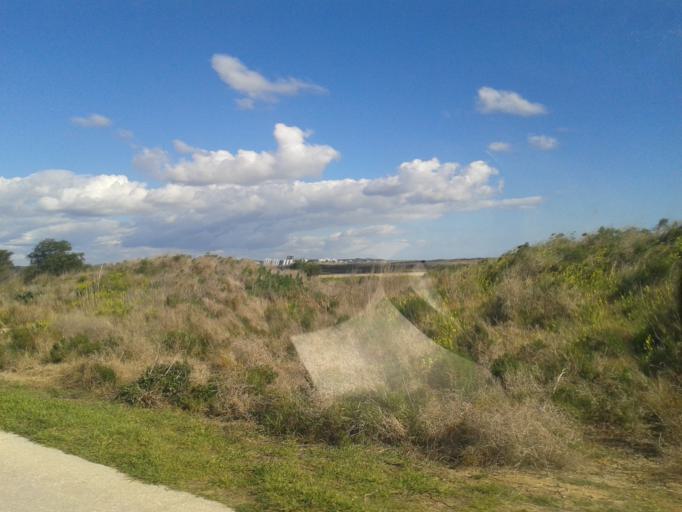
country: PT
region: Faro
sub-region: Lagos
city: Lagos
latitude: 37.1224
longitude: -8.6372
